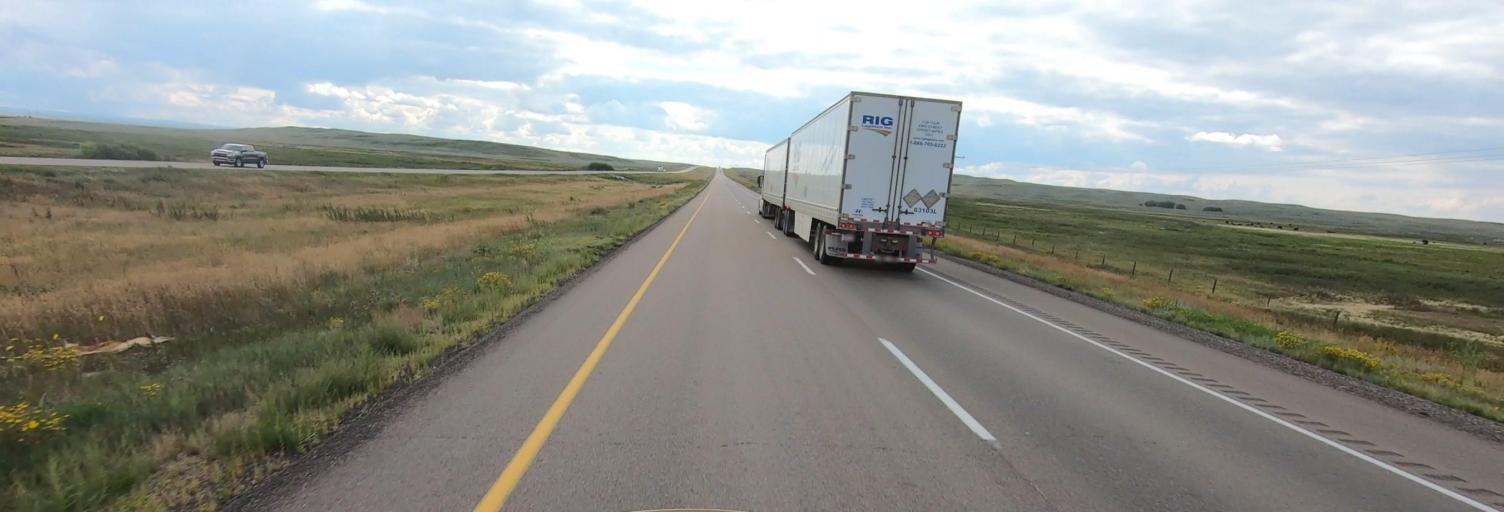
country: CA
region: Saskatchewan
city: Maple Creek
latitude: 50.0398
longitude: -108.9955
